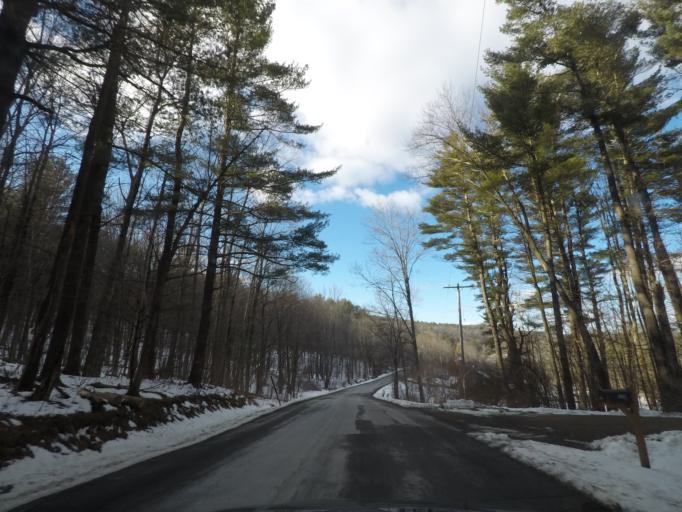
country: US
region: New York
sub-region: Rensselaer County
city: Nassau
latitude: 42.5244
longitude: -73.5267
